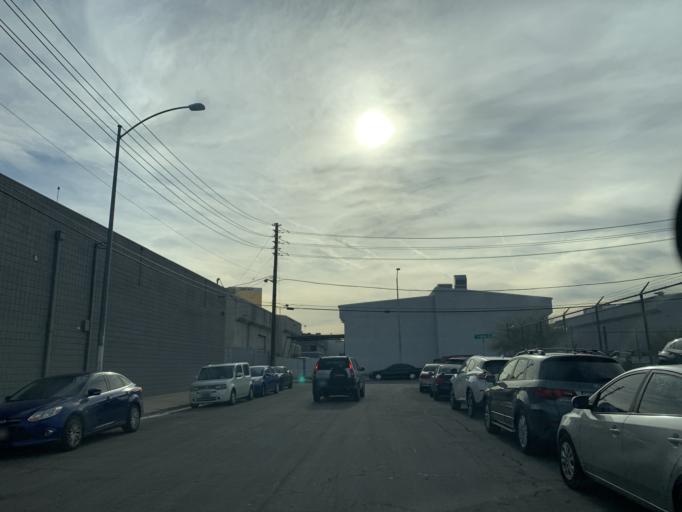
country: US
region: Nevada
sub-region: Clark County
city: Las Vegas
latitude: 36.1410
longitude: -115.1693
